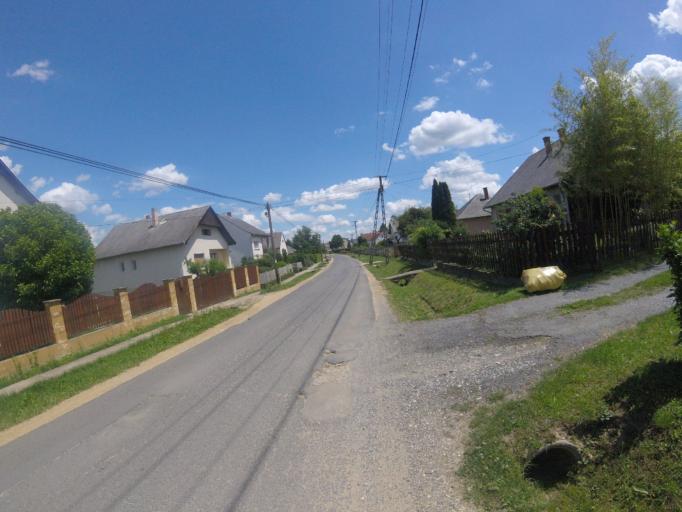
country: HU
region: Zala
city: Zalalovo
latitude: 46.8422
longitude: 16.5817
